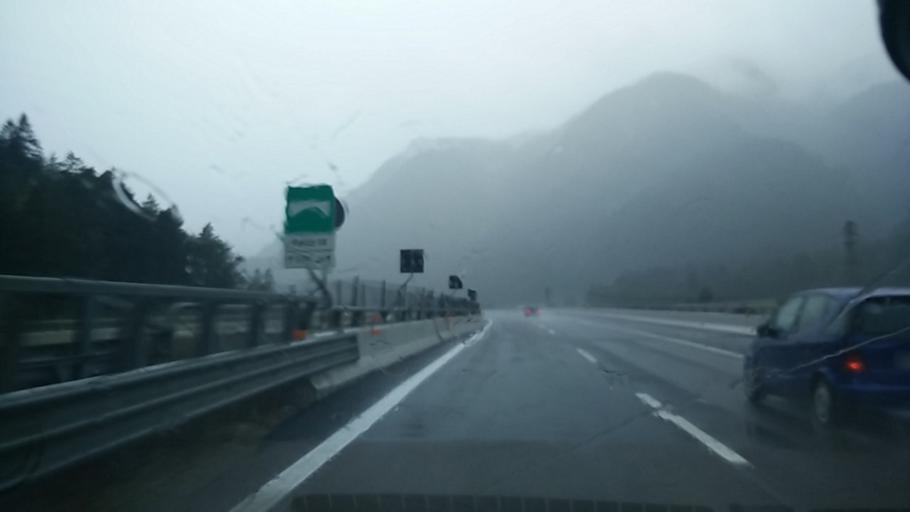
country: IT
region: Friuli Venezia Giulia
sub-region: Provincia di Udine
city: Malborghetto
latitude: 46.5078
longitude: 13.4704
